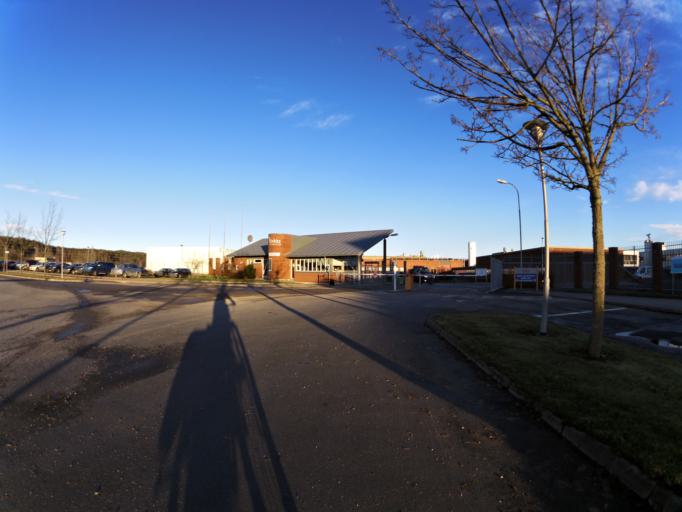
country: NO
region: Ostfold
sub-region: Fredrikstad
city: Fredrikstad
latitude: 59.2419
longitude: 10.9721
